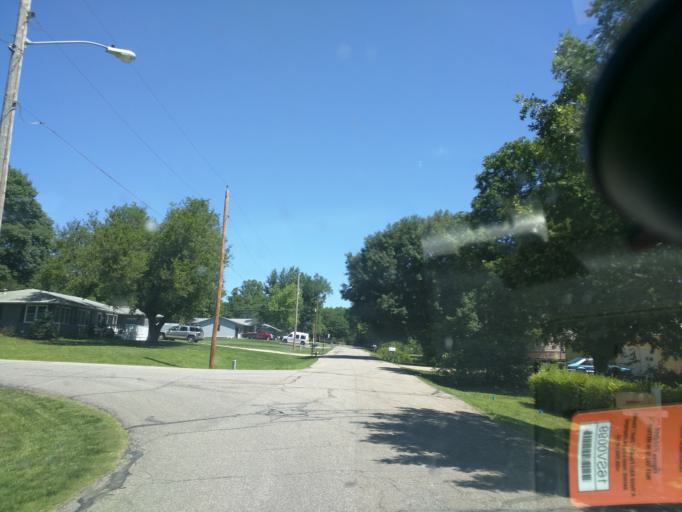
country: US
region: Kansas
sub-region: Riley County
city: Manhattan
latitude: 39.2160
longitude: -96.6099
